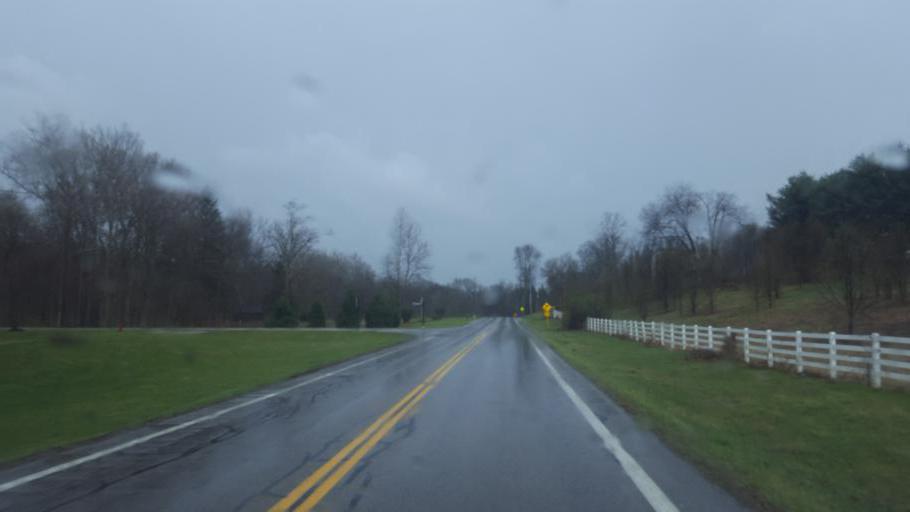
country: US
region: Ohio
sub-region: Delaware County
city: Powell
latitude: 40.1714
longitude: -83.0441
